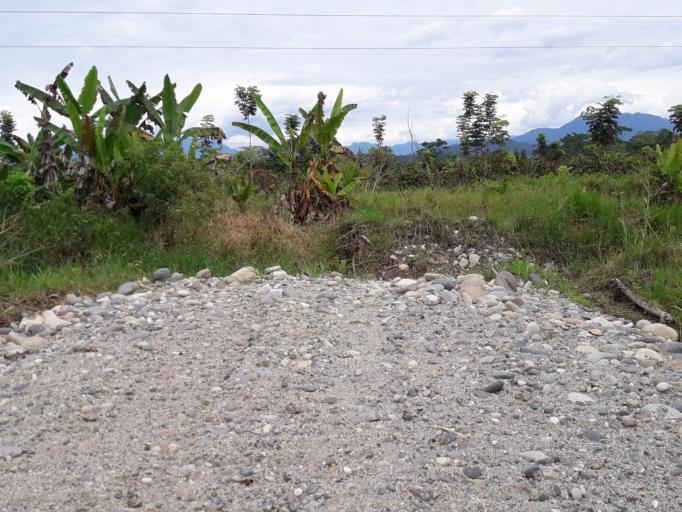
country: EC
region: Napo
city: Tena
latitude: -1.0566
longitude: -77.7940
